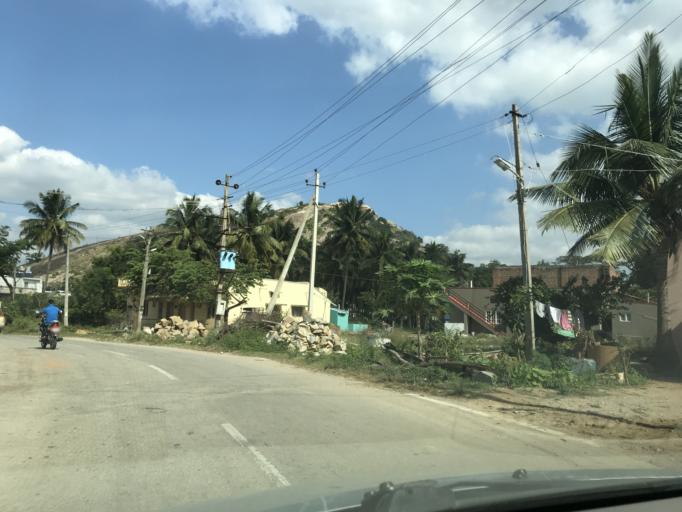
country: IN
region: Karnataka
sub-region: Hassan
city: Shravanabelagola
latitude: 12.8523
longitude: 76.4786
